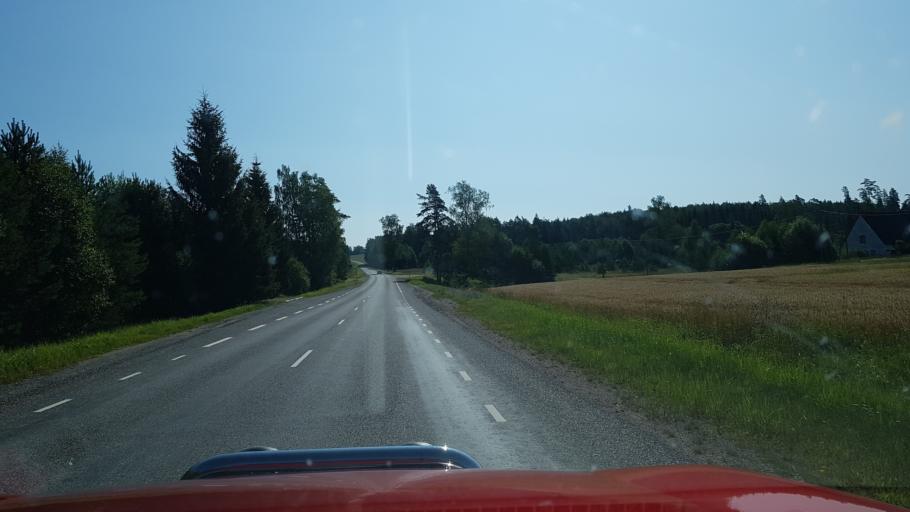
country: EE
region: Vorumaa
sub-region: Voru linn
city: Voru
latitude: 57.9761
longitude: 26.7886
